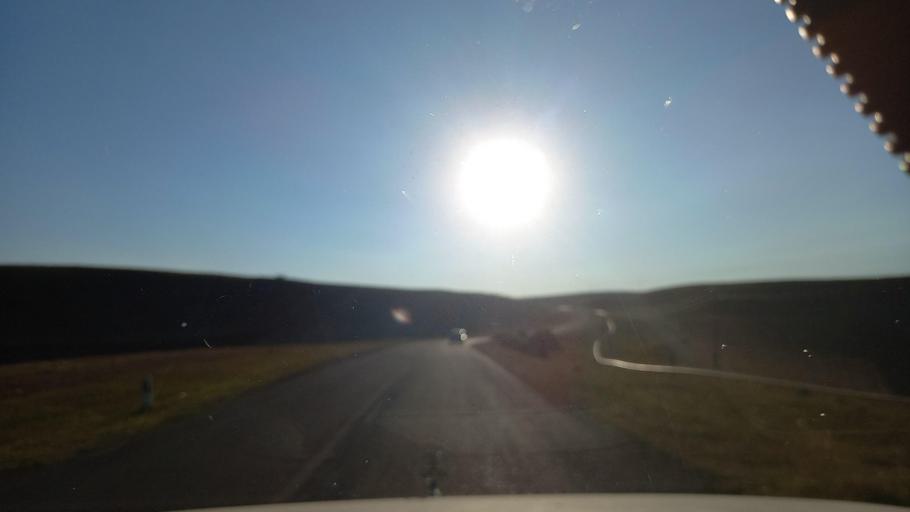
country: AZ
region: Shamkir Rayon
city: Shamkhor
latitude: 40.7637
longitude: 45.9285
